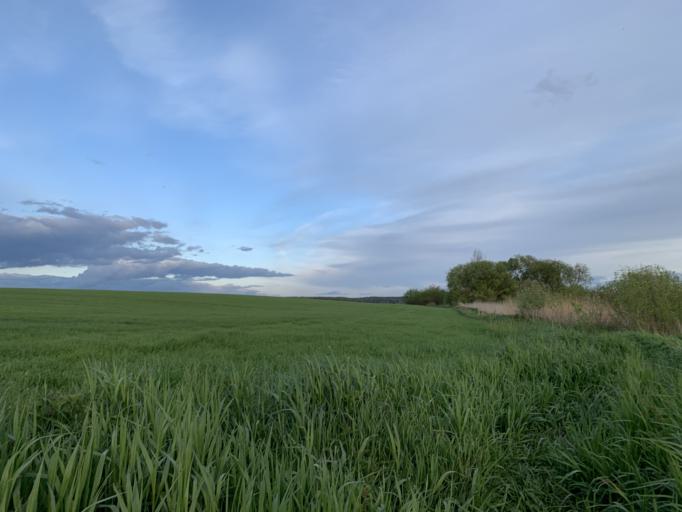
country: BY
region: Minsk
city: Nyasvizh
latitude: 53.2076
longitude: 26.6724
